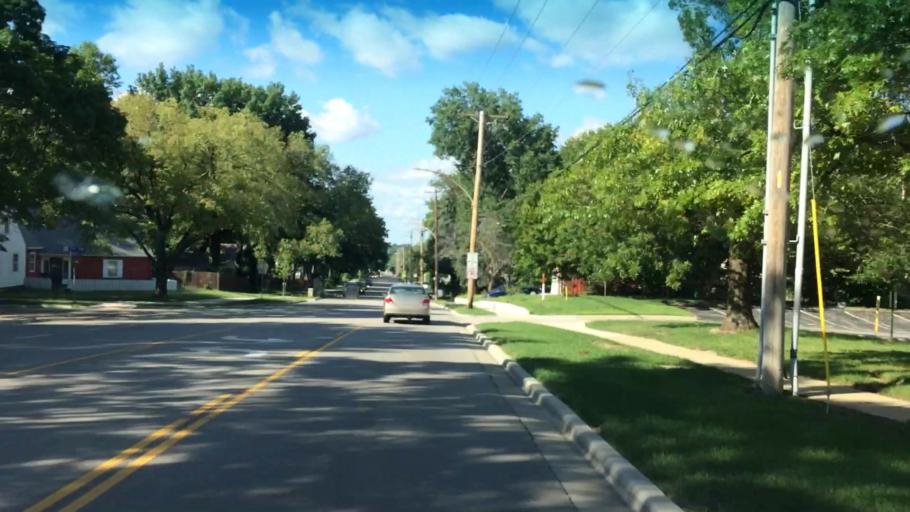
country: US
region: Kansas
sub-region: Johnson County
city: Prairie Village
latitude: 38.9937
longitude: -94.6304
